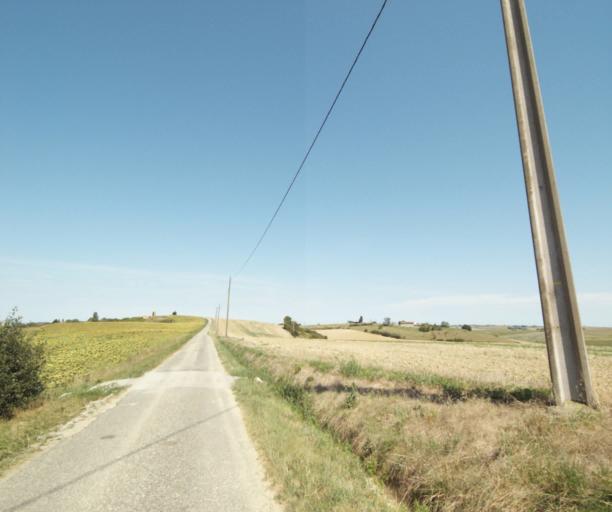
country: FR
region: Midi-Pyrenees
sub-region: Departement de l'Ariege
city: Lezat-sur-Leze
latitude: 43.2653
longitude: 1.3803
